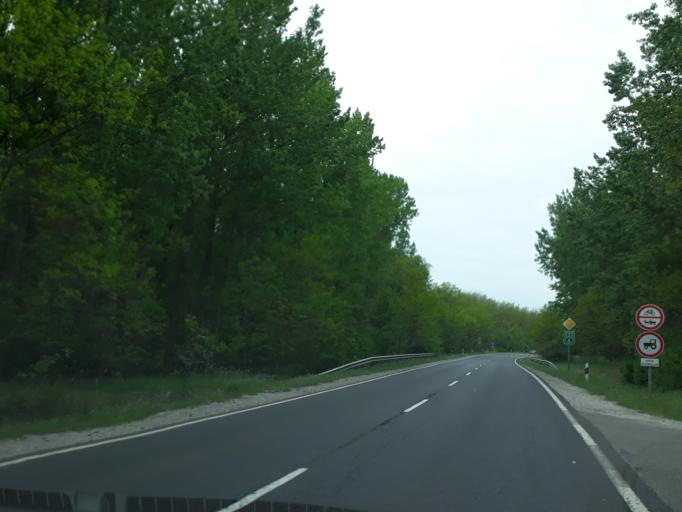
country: HU
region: Szabolcs-Szatmar-Bereg
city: Nyirbogdany
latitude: 48.0537
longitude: 21.9044
